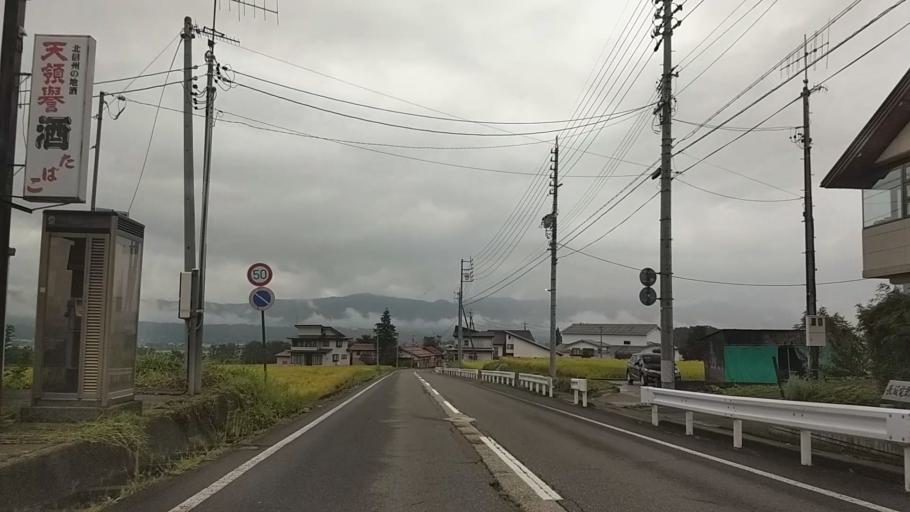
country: JP
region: Nagano
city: Iiyama
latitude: 36.8408
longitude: 138.4069
